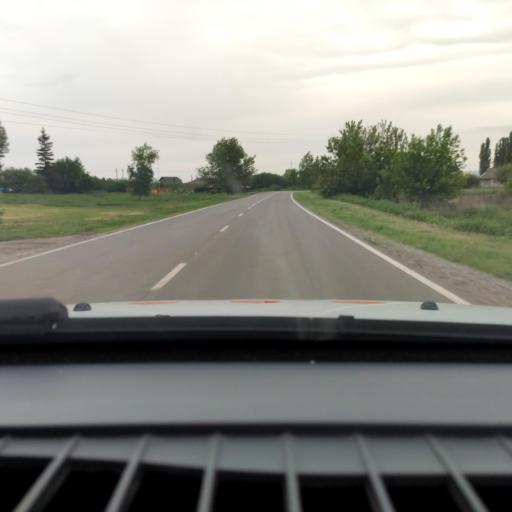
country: RU
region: Voronezj
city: Podkletnoye
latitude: 51.5932
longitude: 39.5226
